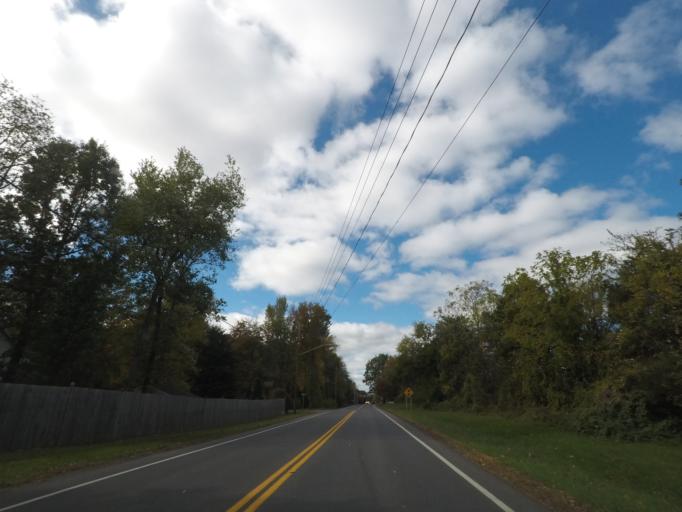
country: US
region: New York
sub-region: Saratoga County
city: Country Knolls
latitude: 42.8556
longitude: -73.7803
